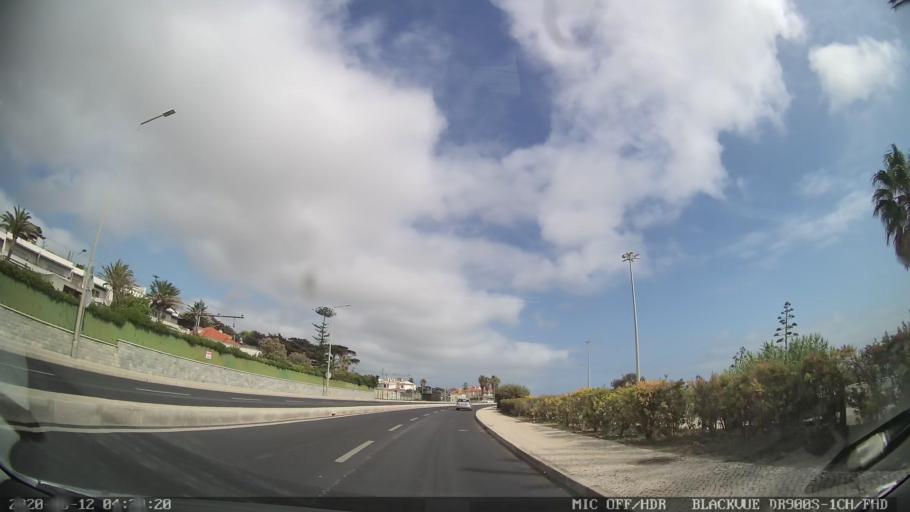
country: PT
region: Lisbon
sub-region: Cascais
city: Parede
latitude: 38.6919
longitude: -9.3662
